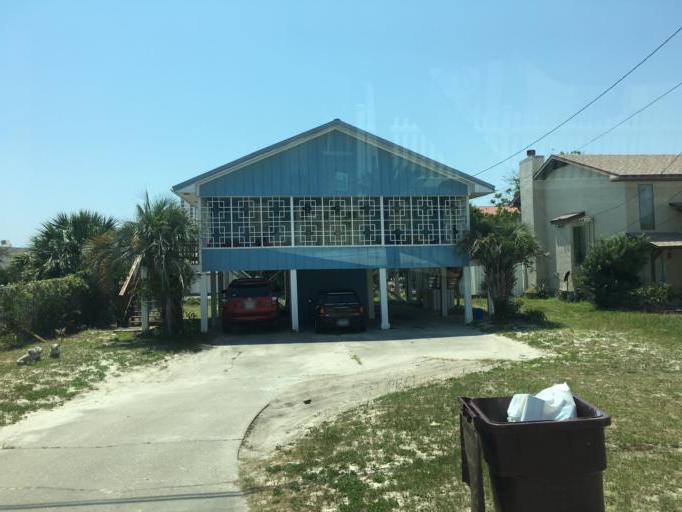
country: US
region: Florida
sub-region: Bay County
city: Laguna Beach
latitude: 30.2254
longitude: -85.8907
